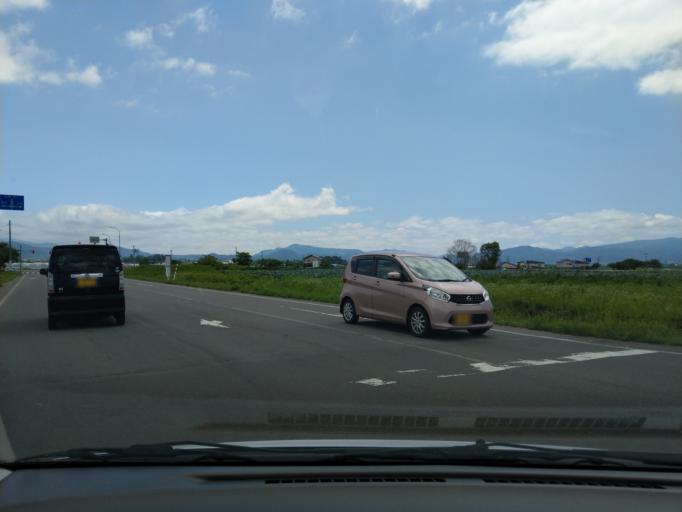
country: JP
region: Aomori
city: Kuroishi
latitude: 40.6319
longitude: 140.5605
